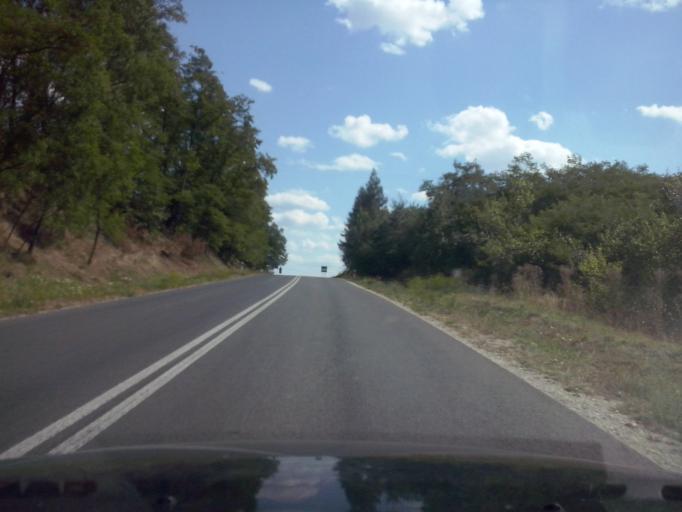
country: PL
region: Swietokrzyskie
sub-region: Powiat staszowski
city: Szydlow
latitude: 50.5872
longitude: 20.9890
